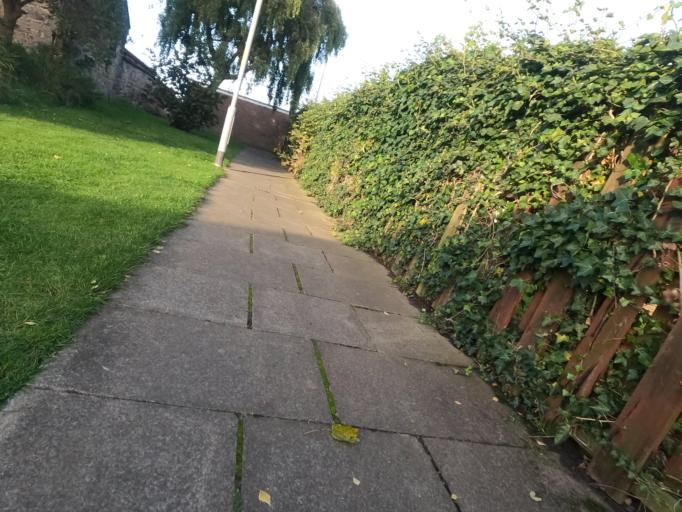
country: GB
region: England
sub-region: Northumberland
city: Seaton Delaval
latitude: 55.0752
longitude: -1.5350
